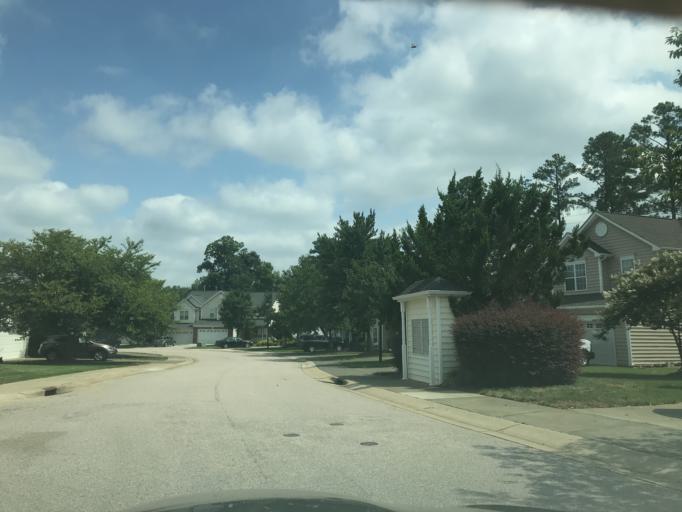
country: US
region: North Carolina
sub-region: Wake County
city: Wake Forest
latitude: 35.9299
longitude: -78.5598
